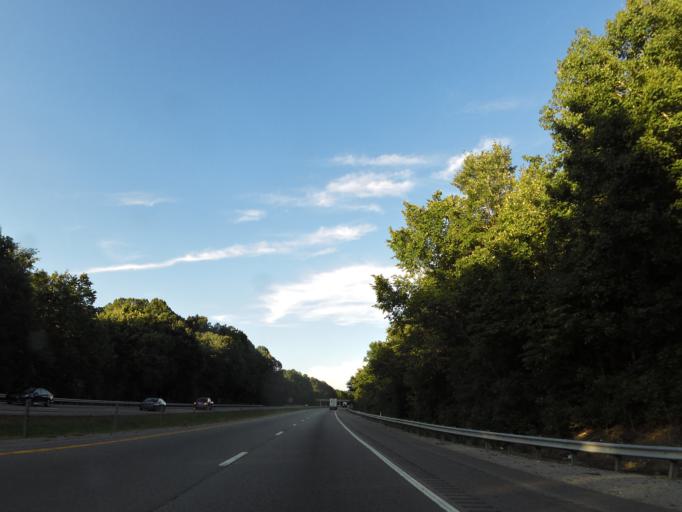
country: US
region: Tennessee
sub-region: Putnam County
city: Lafayette
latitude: 36.0939
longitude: -85.7164
